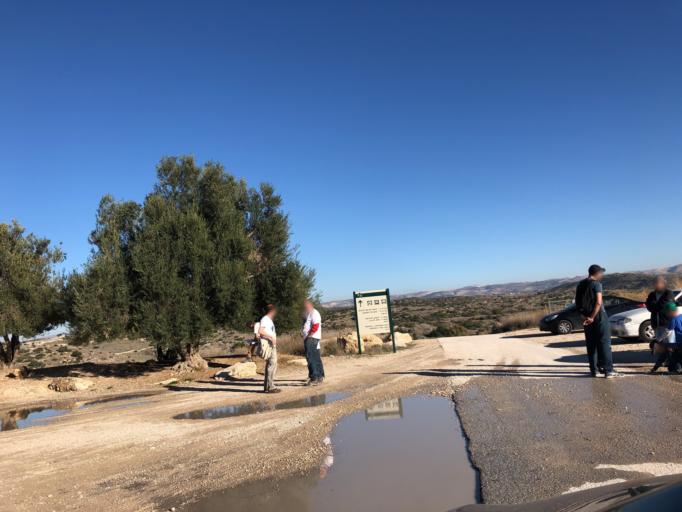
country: PS
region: West Bank
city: Idhna
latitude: 31.5920
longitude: 34.9000
